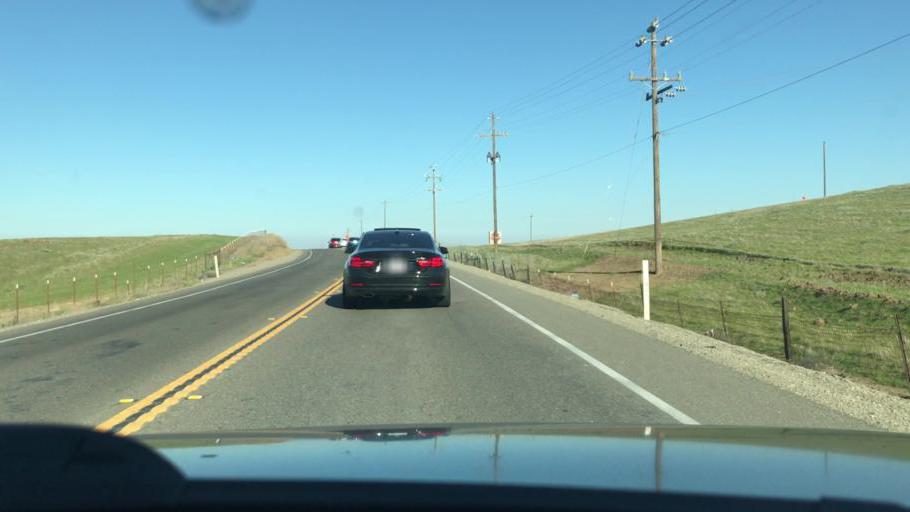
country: US
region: California
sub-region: San Joaquin County
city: Mountain House
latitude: 37.7416
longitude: -121.6078
